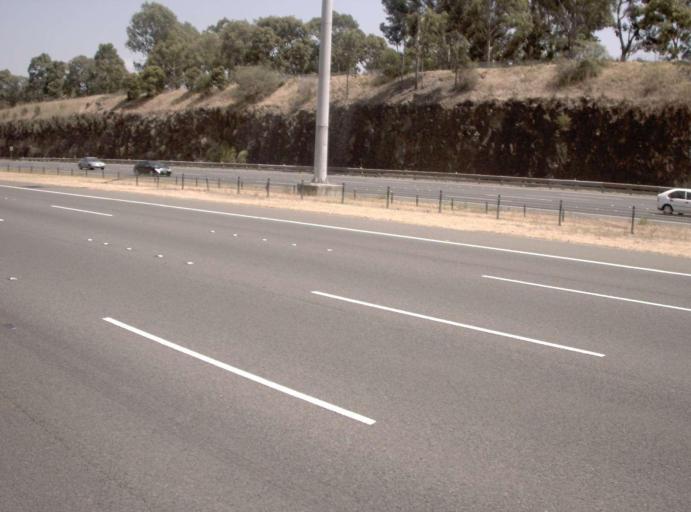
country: AU
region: Victoria
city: Abbotsford
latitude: -37.7929
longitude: 145.0094
